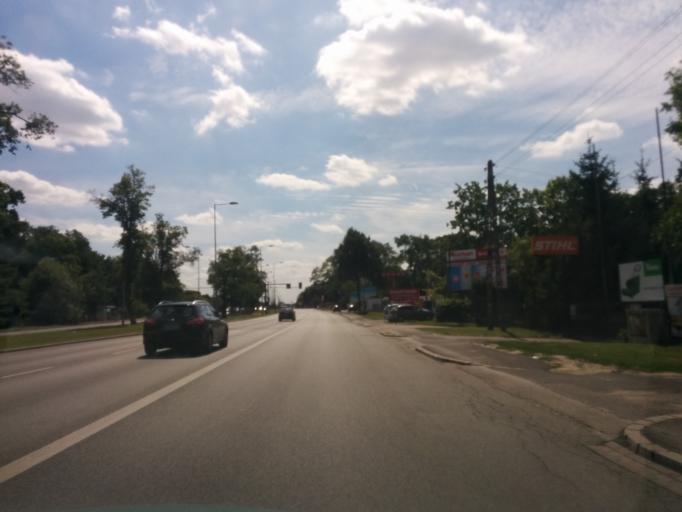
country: PL
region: Masovian Voivodeship
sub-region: Warszawa
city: Bialoleka
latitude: 52.3254
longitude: 20.9689
